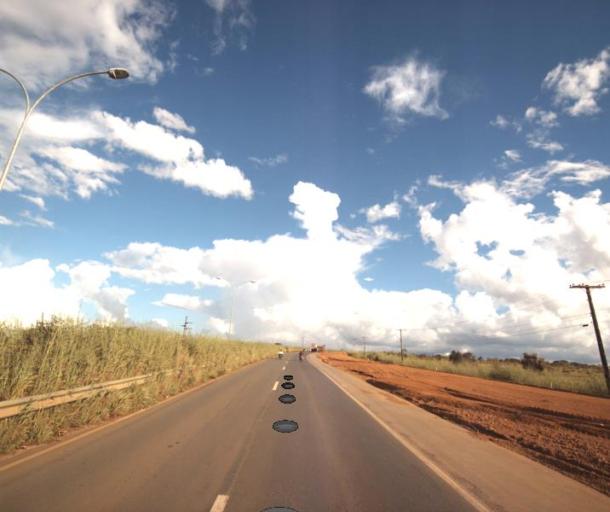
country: BR
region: Goias
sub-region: Anapolis
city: Anapolis
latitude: -16.3117
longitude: -48.9224
